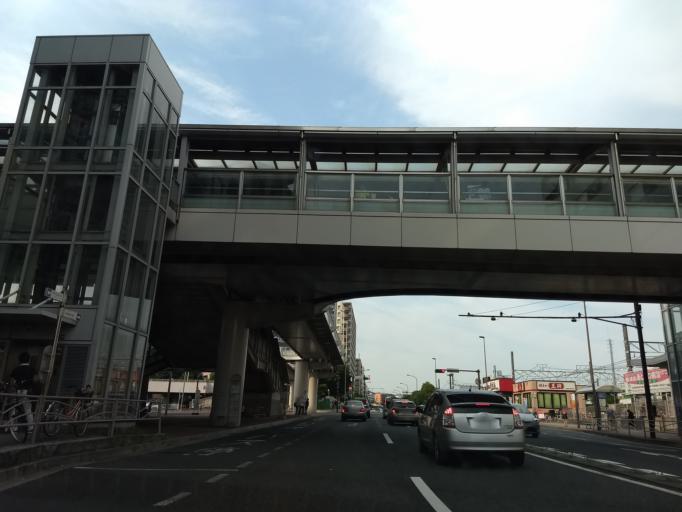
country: JP
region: Kanagawa
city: Yokohama
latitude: 35.4780
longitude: 139.6325
